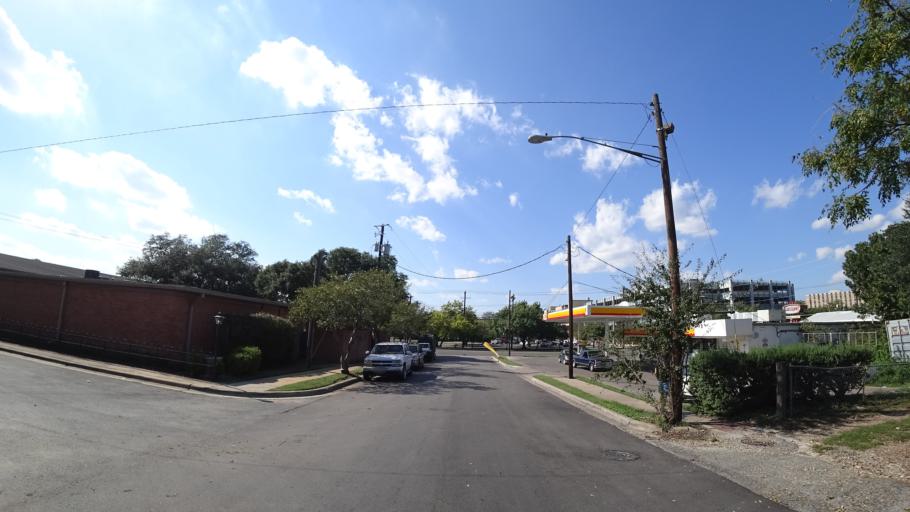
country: US
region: Texas
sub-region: Travis County
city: Austin
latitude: 30.3012
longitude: -97.7449
